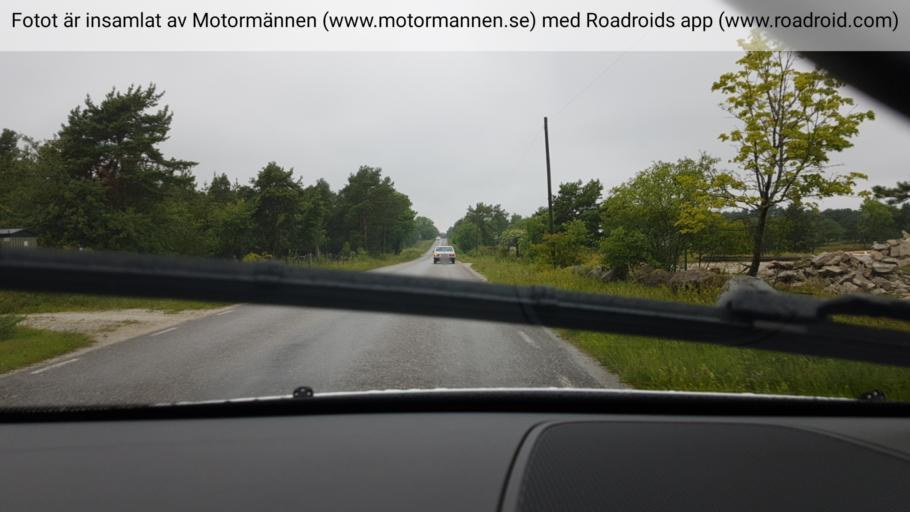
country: SE
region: Gotland
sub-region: Gotland
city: Slite
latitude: 57.8564
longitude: 19.0236
